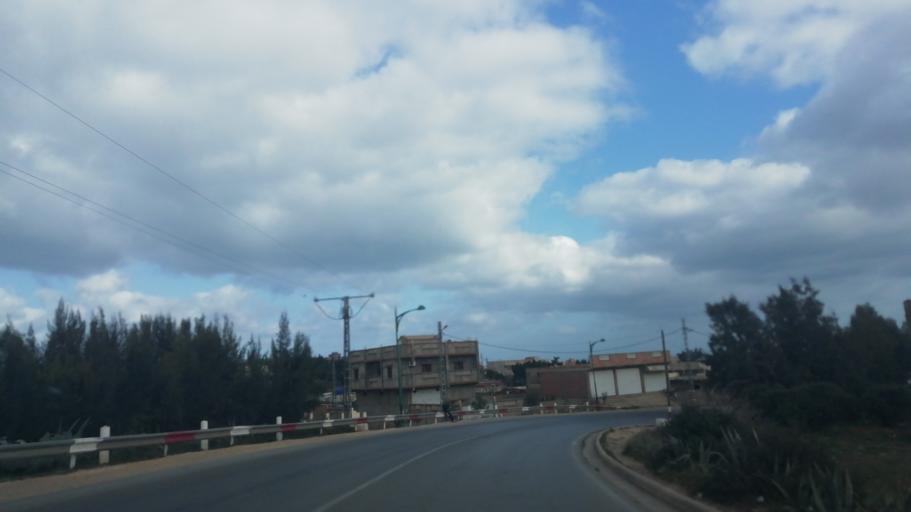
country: DZ
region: Relizane
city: Mazouna
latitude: 36.2843
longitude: 0.6442
